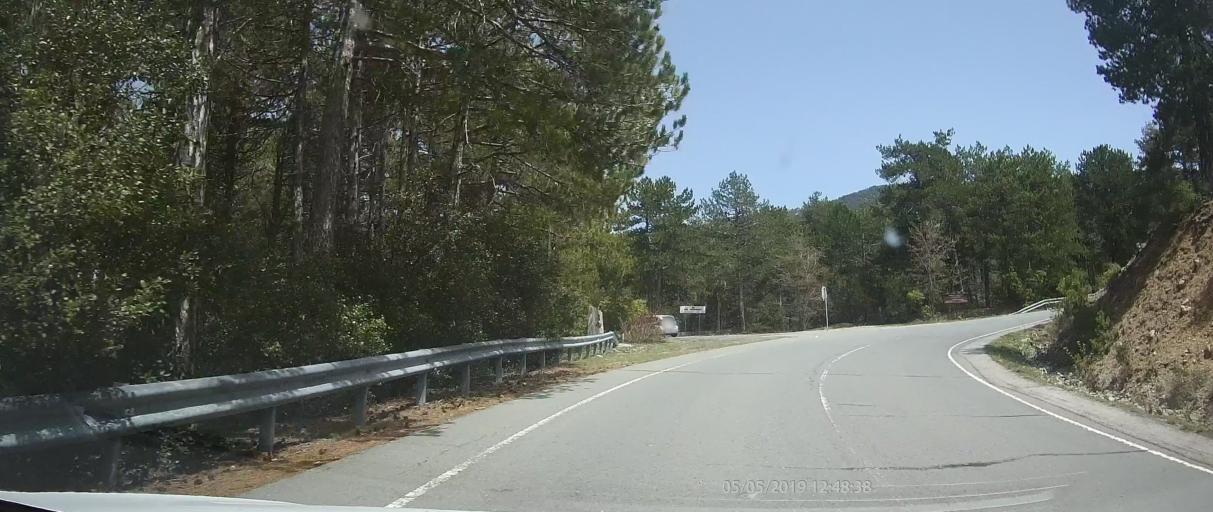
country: CY
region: Lefkosia
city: Kakopetria
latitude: 34.9597
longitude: 32.8369
